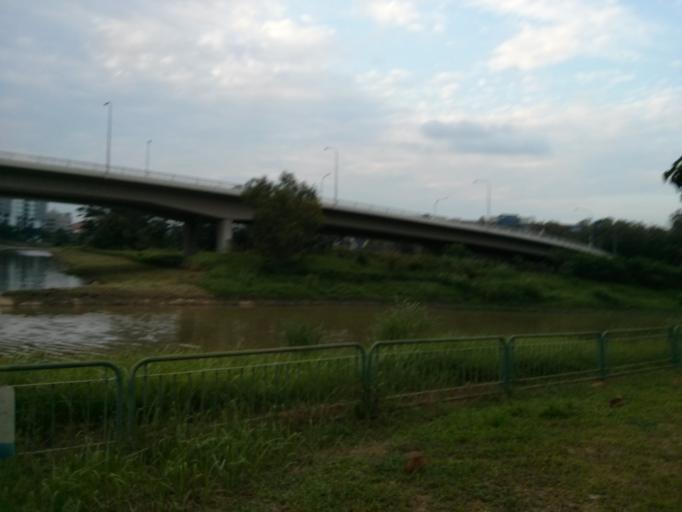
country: SG
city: Singapore
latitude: 1.3224
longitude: 103.7524
